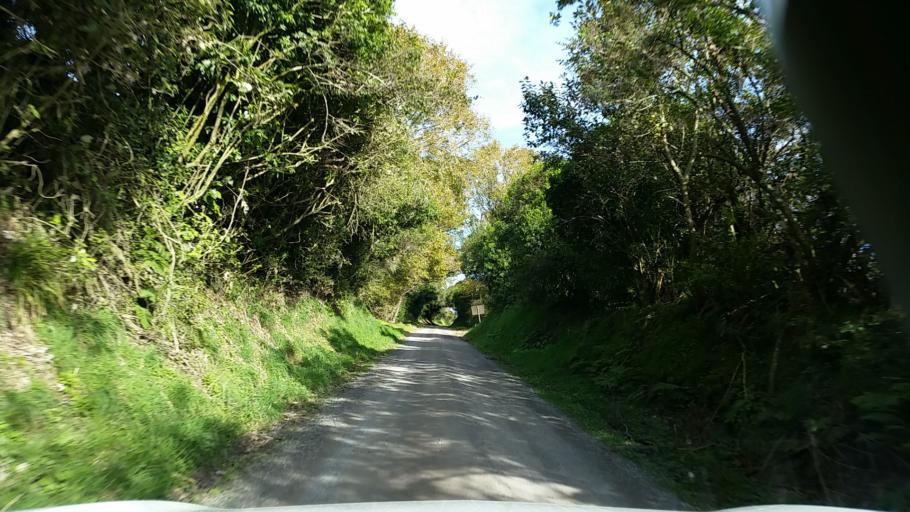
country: NZ
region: Bay of Plenty
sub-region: Rotorua District
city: Rotorua
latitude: -38.2416
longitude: 176.3457
